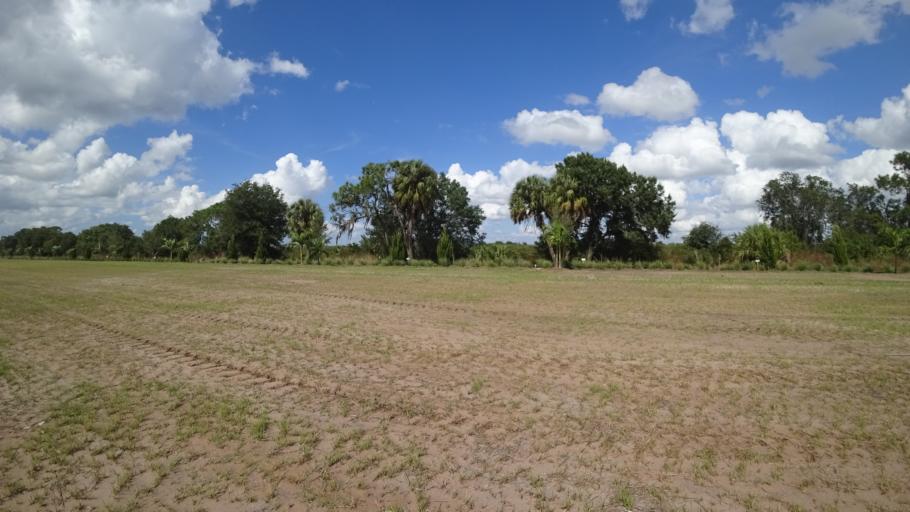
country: US
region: Florida
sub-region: Sarasota County
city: The Meadows
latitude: 27.4525
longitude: -82.3663
